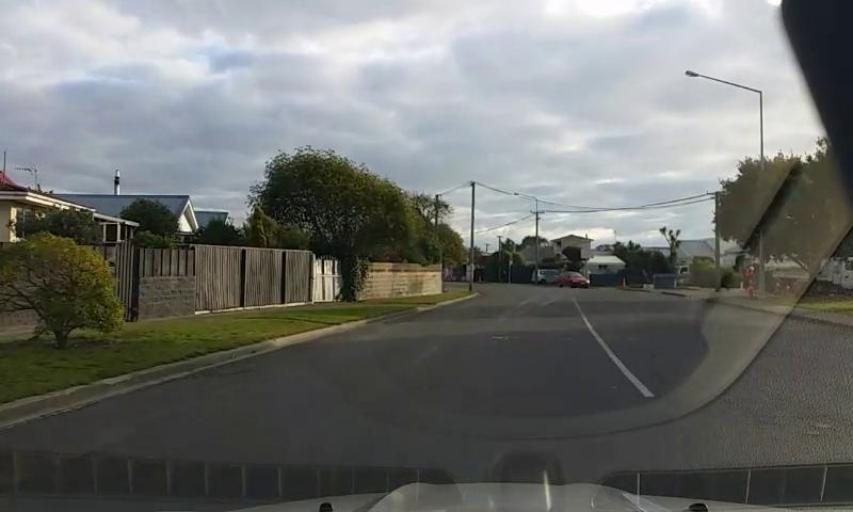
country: NZ
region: Canterbury
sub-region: Christchurch City
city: Christchurch
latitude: -43.5192
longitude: 172.7309
